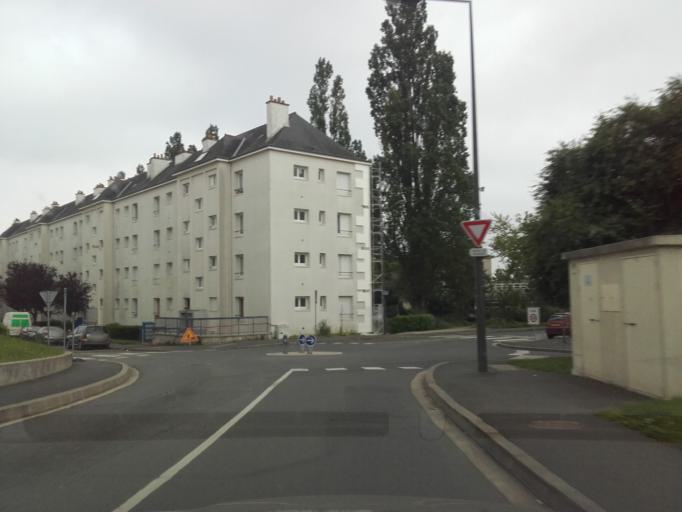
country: FR
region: Centre
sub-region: Departement d'Indre-et-Loire
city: Saint-Cyr-sur-Loire
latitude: 47.4137
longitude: 0.6871
